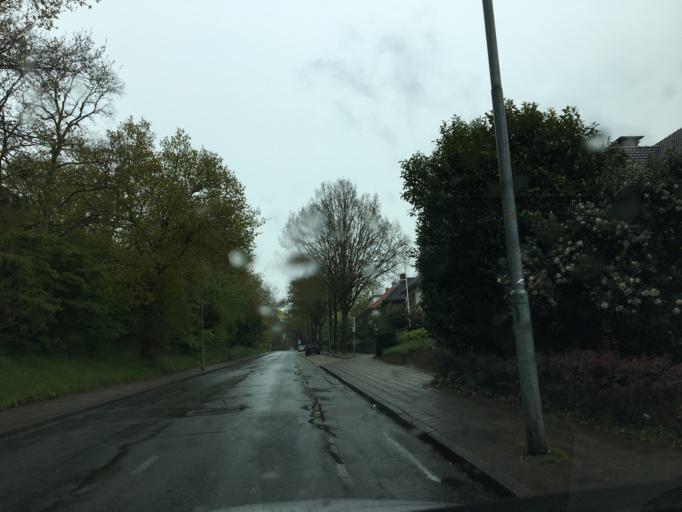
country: NL
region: Gelderland
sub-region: Gemeente Ede
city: Ede
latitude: 52.0431
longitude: 5.6751
